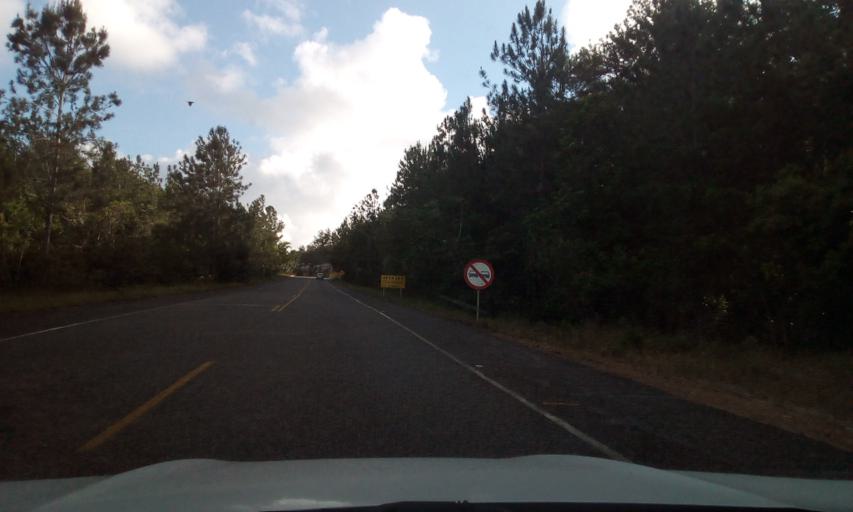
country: BR
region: Bahia
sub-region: Conde
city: Conde
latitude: -12.0980
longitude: -37.7754
